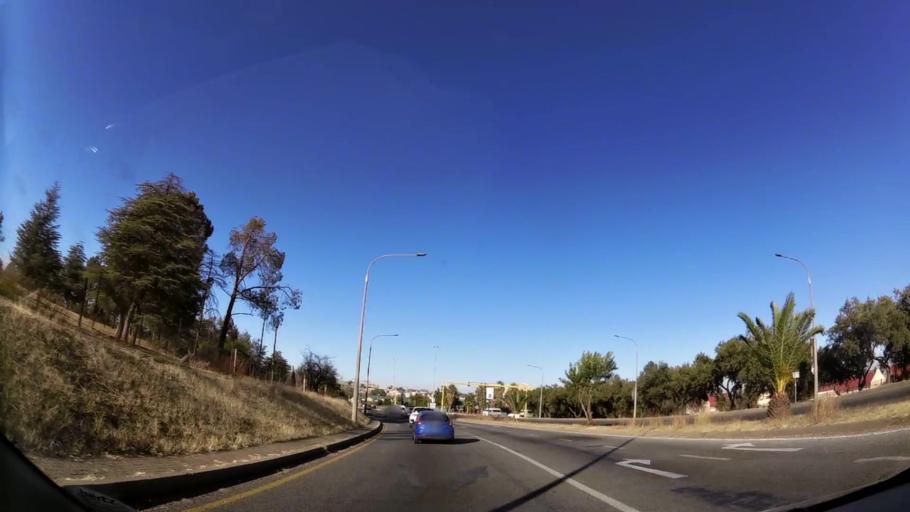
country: ZA
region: Gauteng
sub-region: West Rand District Municipality
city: Krugersdorp
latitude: -26.0934
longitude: 27.7781
